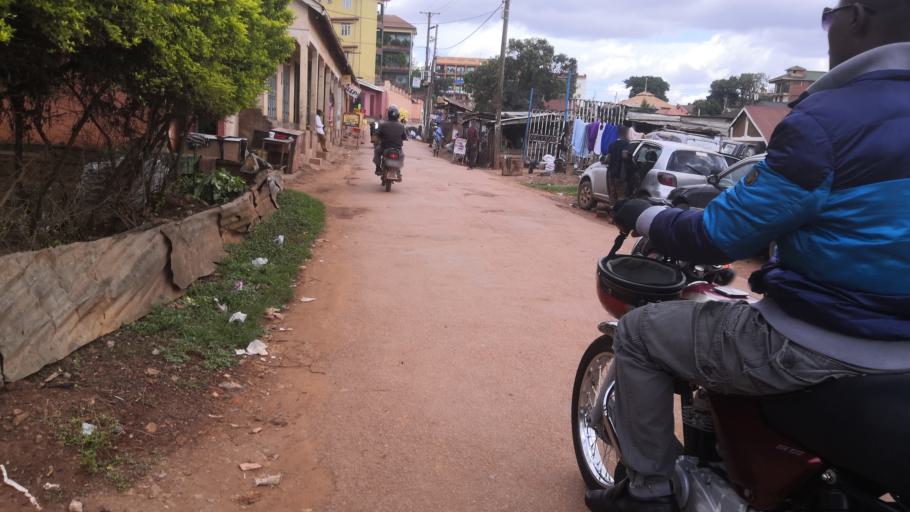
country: UG
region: Central Region
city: Kampala Central Division
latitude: 0.3292
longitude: 32.5633
